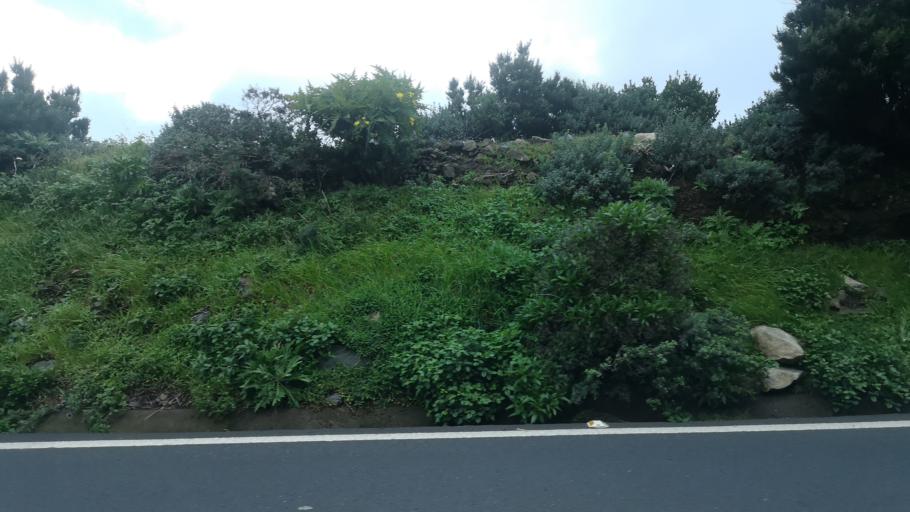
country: ES
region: Canary Islands
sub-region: Provincia de Santa Cruz de Tenerife
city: Alajero
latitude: 28.1064
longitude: -17.2132
